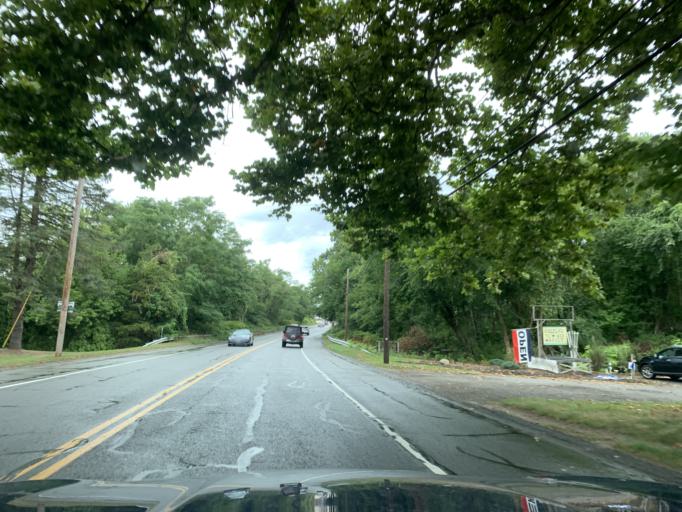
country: US
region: Rhode Island
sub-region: Bristol County
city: Warren
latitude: 41.7657
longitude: -71.2679
